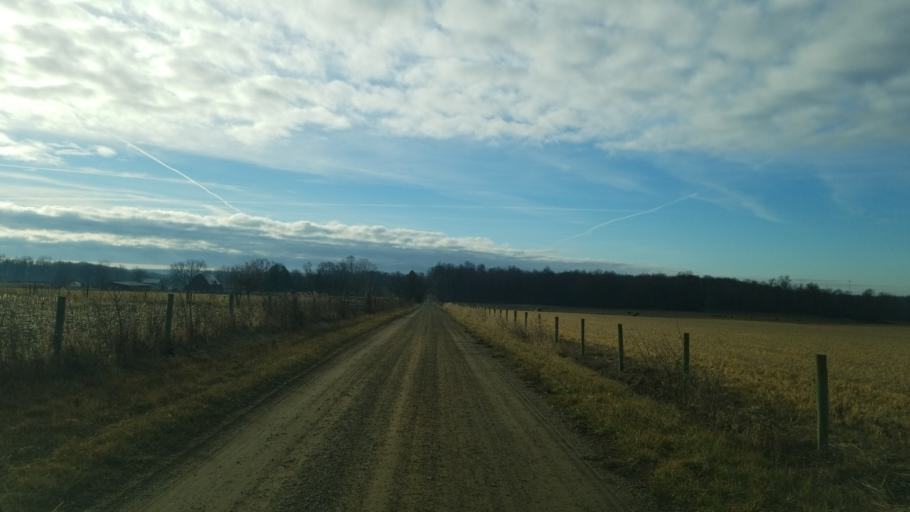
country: US
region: Ohio
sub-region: Knox County
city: Gambier
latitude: 40.3200
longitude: -82.3211
